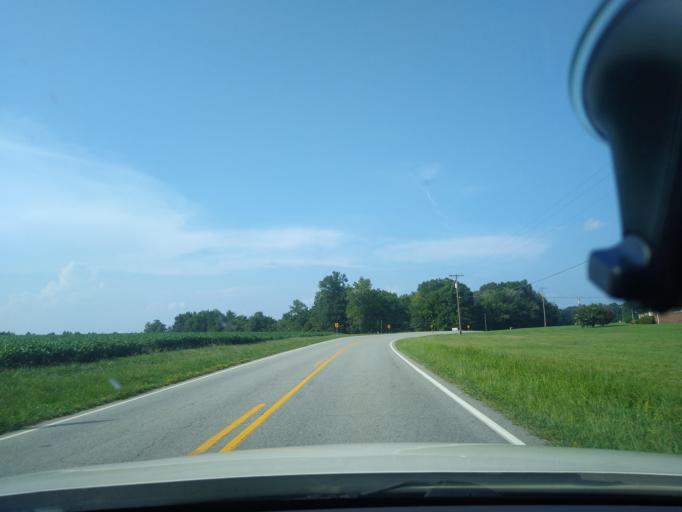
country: US
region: North Carolina
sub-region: Guilford County
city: McLeansville
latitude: 36.0930
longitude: -79.6774
